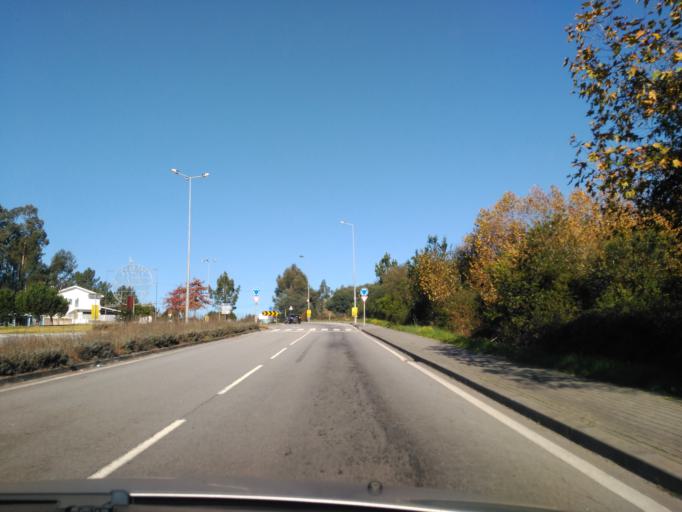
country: PT
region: Braga
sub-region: Braga
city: Adaufe
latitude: 41.5807
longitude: -8.3699
